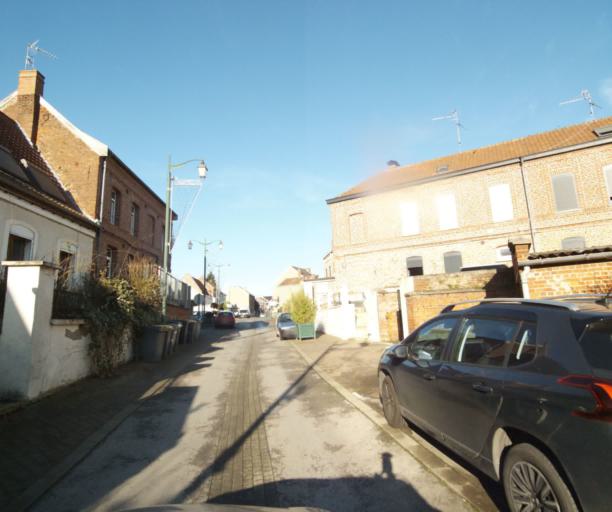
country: FR
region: Nord-Pas-de-Calais
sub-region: Departement du Nord
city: Aulnoy-lez-Valenciennes
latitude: 50.3325
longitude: 3.5284
